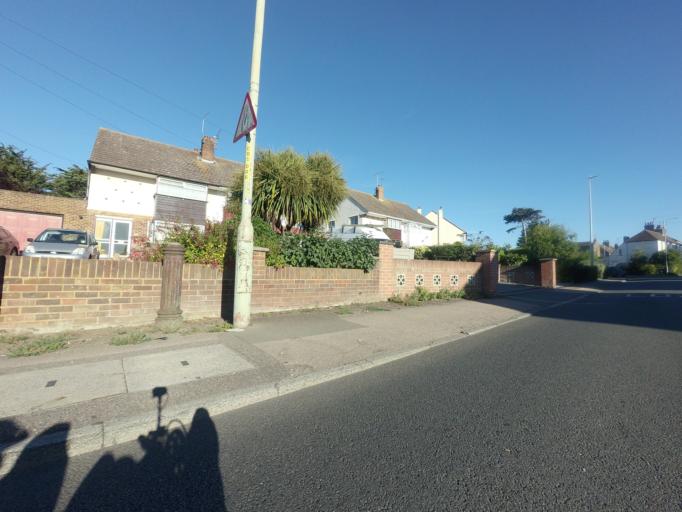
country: GB
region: England
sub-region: Kent
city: Herne Bay
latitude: 51.3610
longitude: 1.1311
